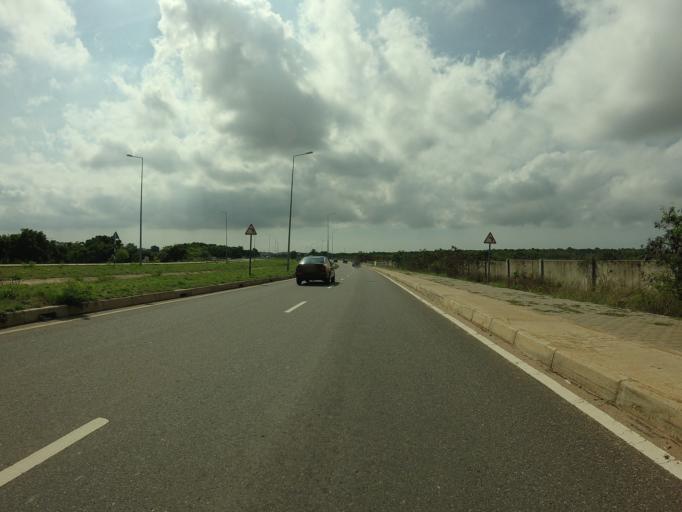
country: GH
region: Greater Accra
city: Medina Estates
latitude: 5.6144
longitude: -0.1536
